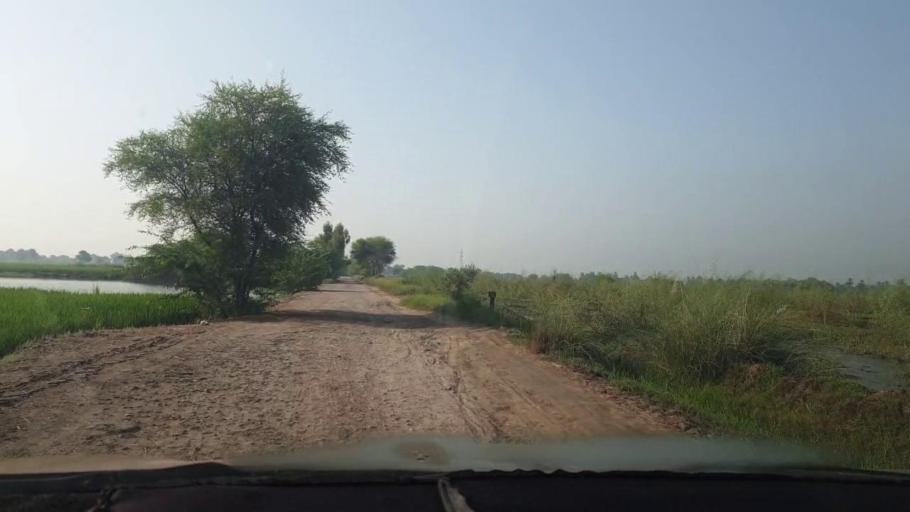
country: PK
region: Sindh
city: Kambar
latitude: 27.5790
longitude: 68.1017
